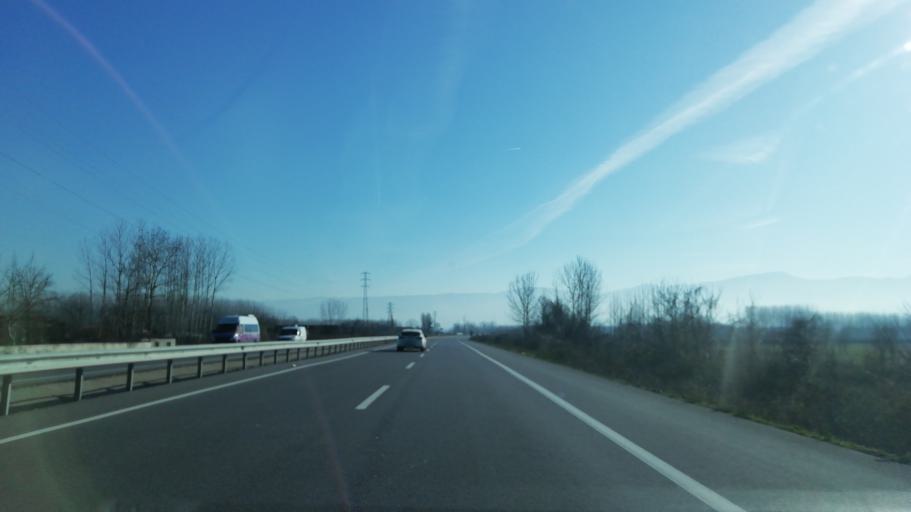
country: TR
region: Sakarya
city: Akyazi
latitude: 40.7085
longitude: 30.5655
